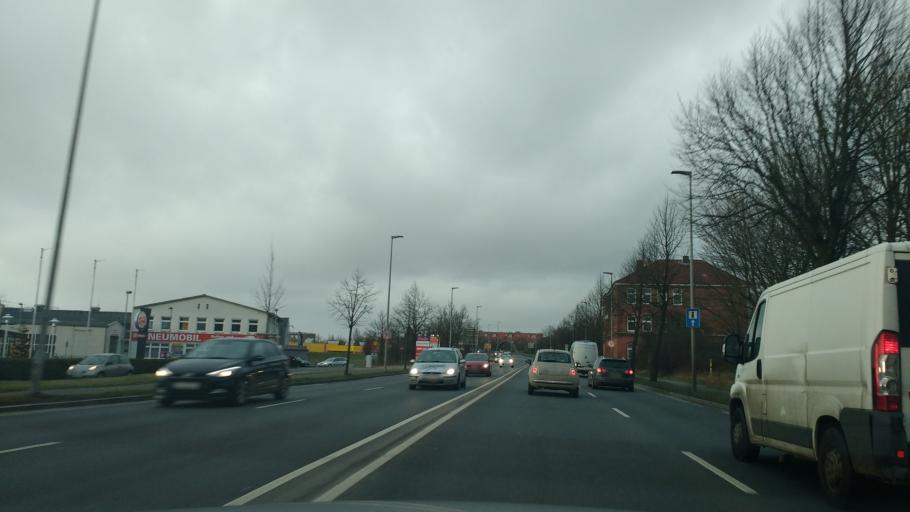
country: DE
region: Schleswig-Holstein
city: Itzehoe
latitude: 53.9148
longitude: 9.5159
